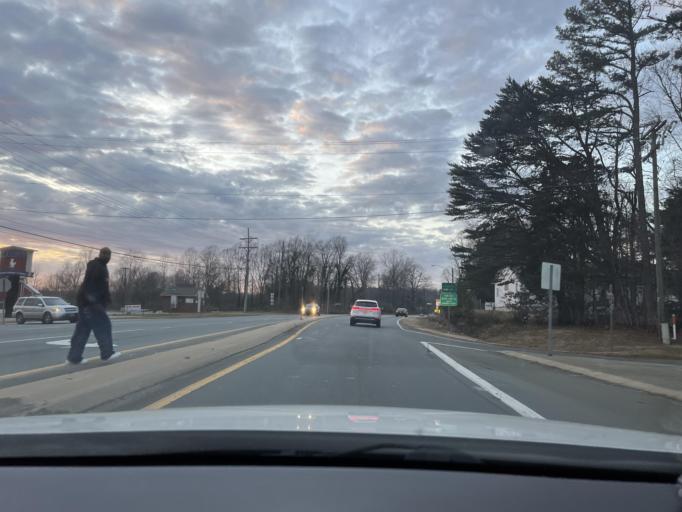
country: US
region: North Carolina
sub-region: Guilford County
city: McLeansville
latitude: 36.0633
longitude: -79.6094
